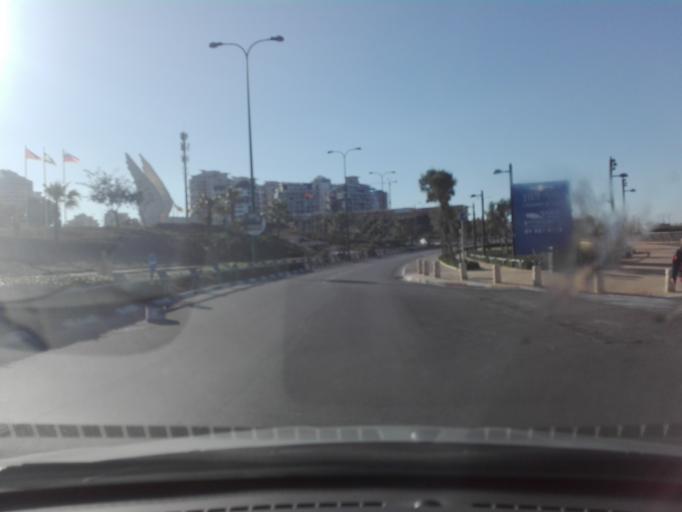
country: IL
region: Central District
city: Netanya
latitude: 32.3031
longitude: 34.8430
